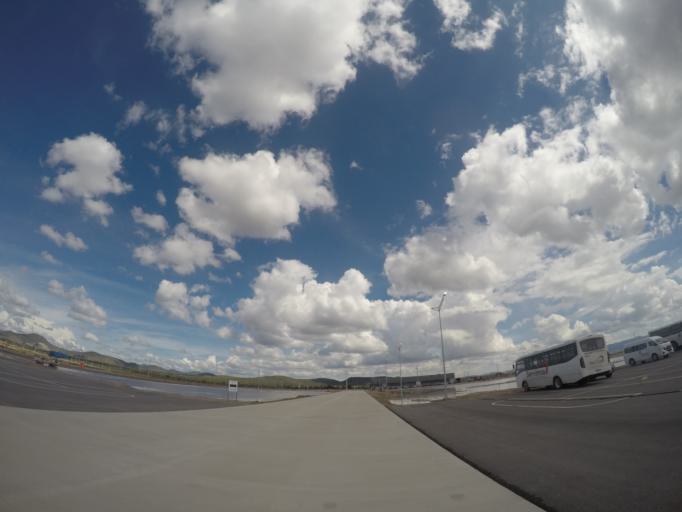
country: MX
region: San Luis Potosi
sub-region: Zaragoza
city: Cerro Gordo
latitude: 21.9661
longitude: -100.8458
